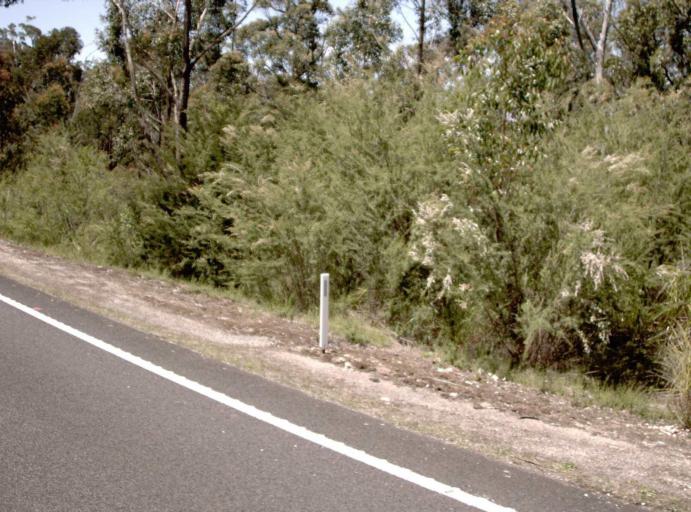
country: AU
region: Victoria
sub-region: East Gippsland
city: Lakes Entrance
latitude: -37.6965
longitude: 148.6115
